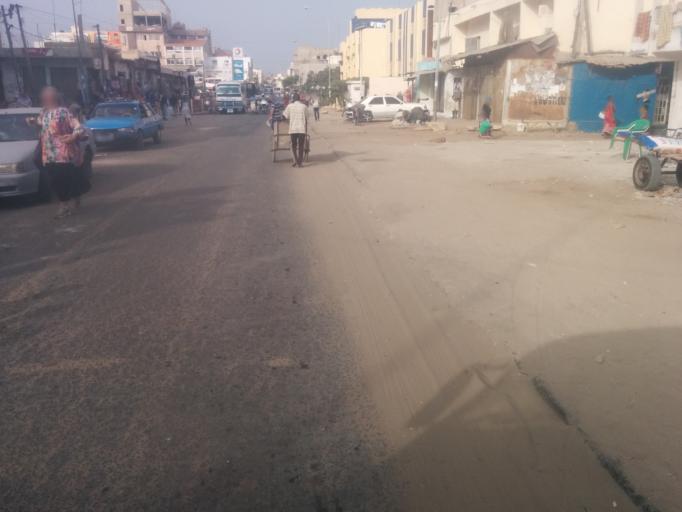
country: SN
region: Dakar
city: Grand Dakar
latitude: 14.7595
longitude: -17.4454
